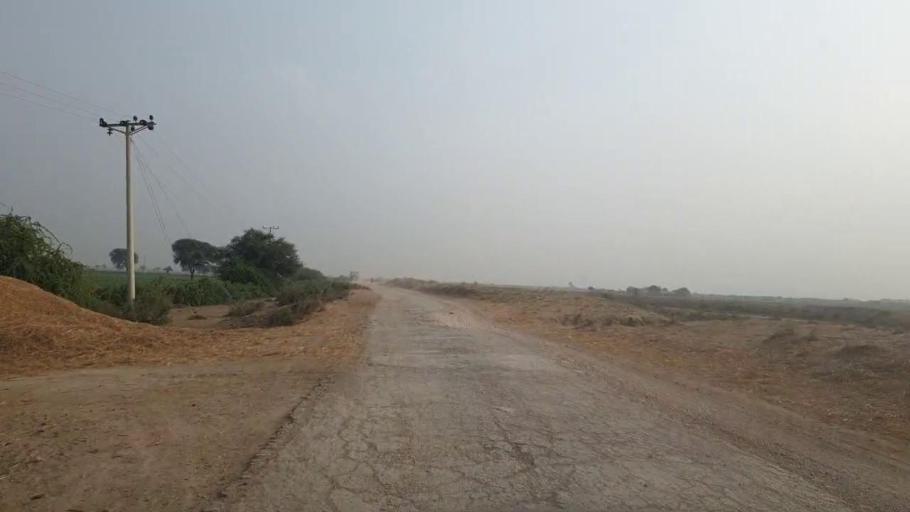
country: PK
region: Sindh
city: Mirpur Batoro
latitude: 24.5701
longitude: 68.3985
